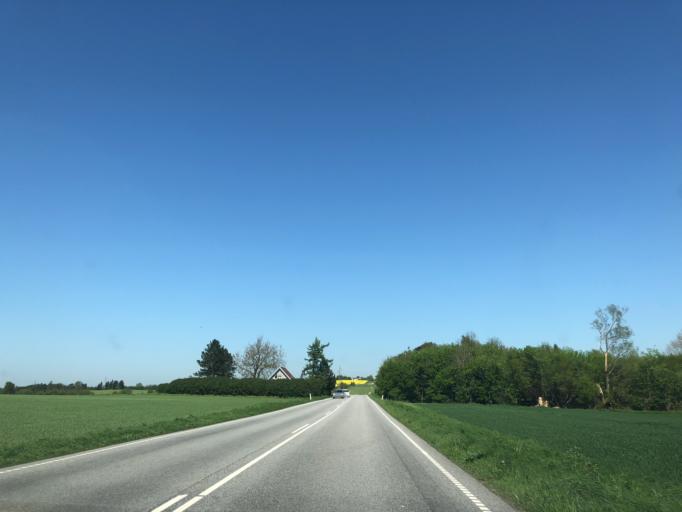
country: DK
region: Zealand
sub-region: Slagelse Kommune
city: Skaelskor
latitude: 55.3159
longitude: 11.2972
